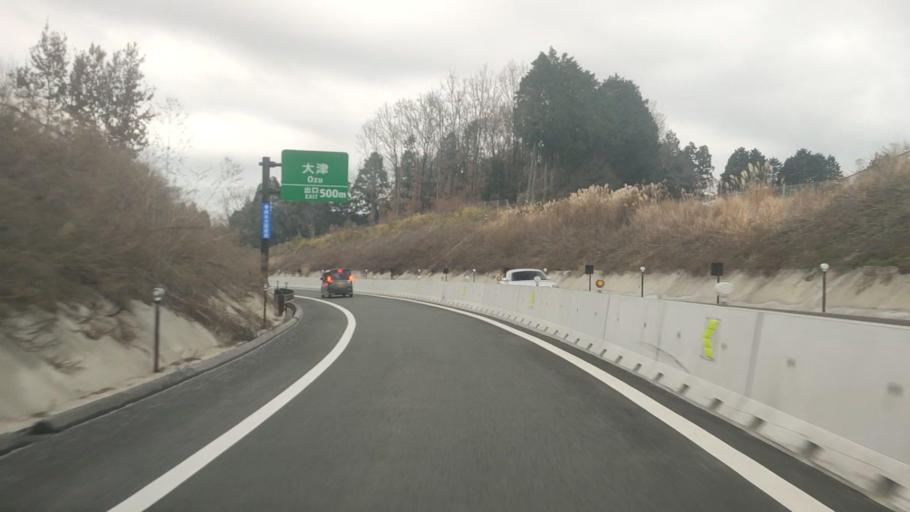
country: JP
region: Kumamoto
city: Ozu
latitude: 32.8964
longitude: 130.8966
